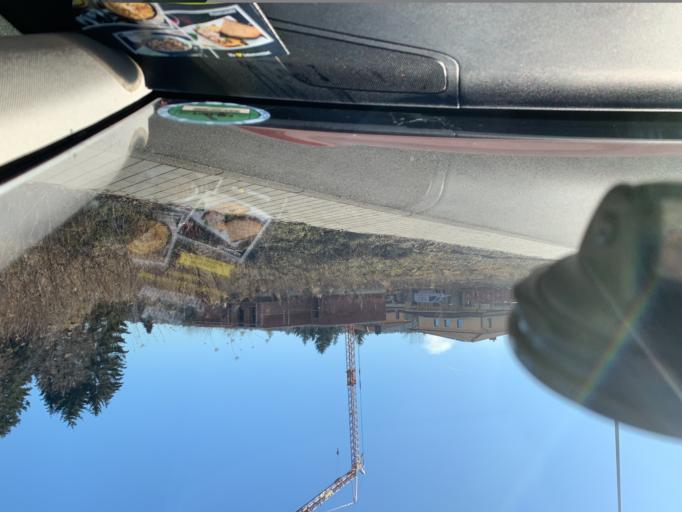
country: DE
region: Baden-Wuerttemberg
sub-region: Karlsruhe Region
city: Pforzheim
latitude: 48.8806
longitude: 8.7099
